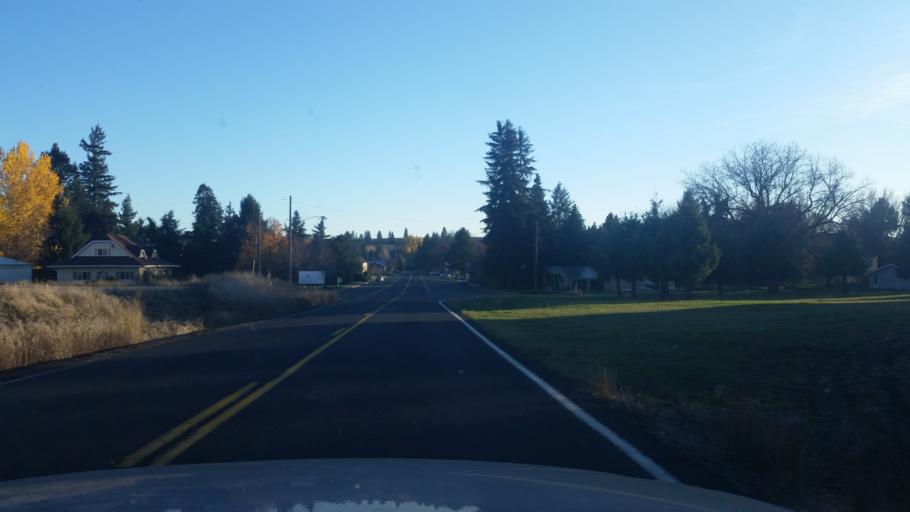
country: US
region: Washington
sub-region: Spokane County
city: Opportunity
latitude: 47.3455
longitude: -117.2278
